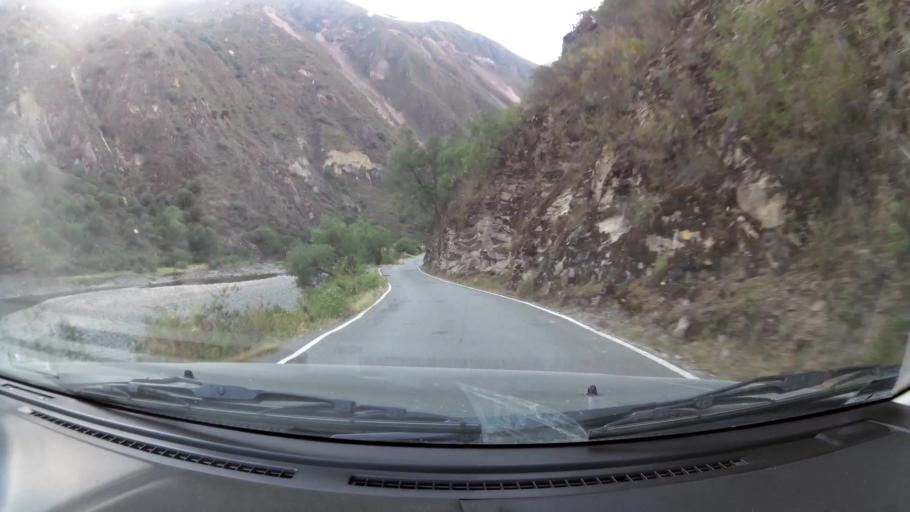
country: PE
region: Huancavelica
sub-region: Provincia de Churcampa
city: La Esmeralda
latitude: -12.5584
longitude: -74.7092
